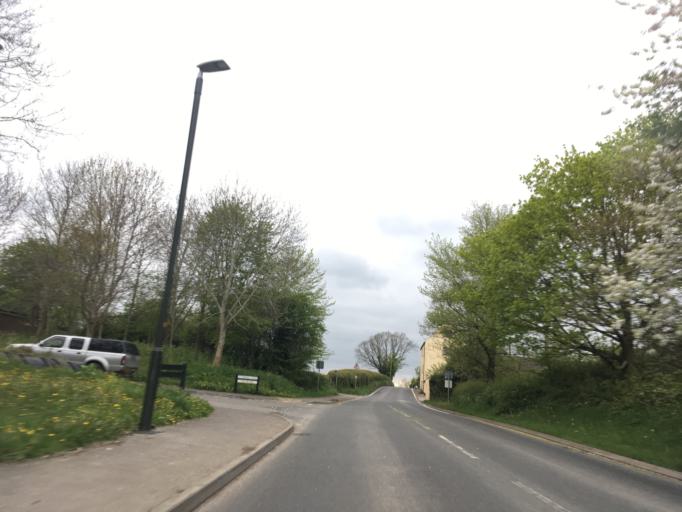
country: GB
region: England
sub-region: Gloucestershire
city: Wotton-under-Edge
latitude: 51.6272
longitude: -2.3700
